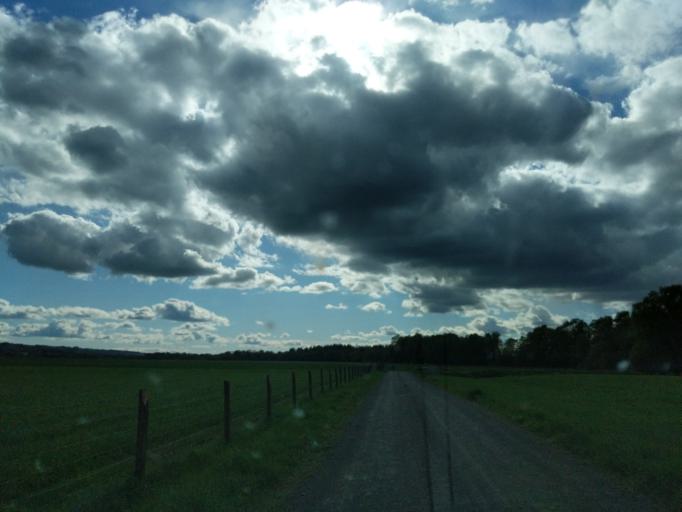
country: GB
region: Scotland
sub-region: Stirling
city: Callander
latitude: 56.1547
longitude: -4.1691
